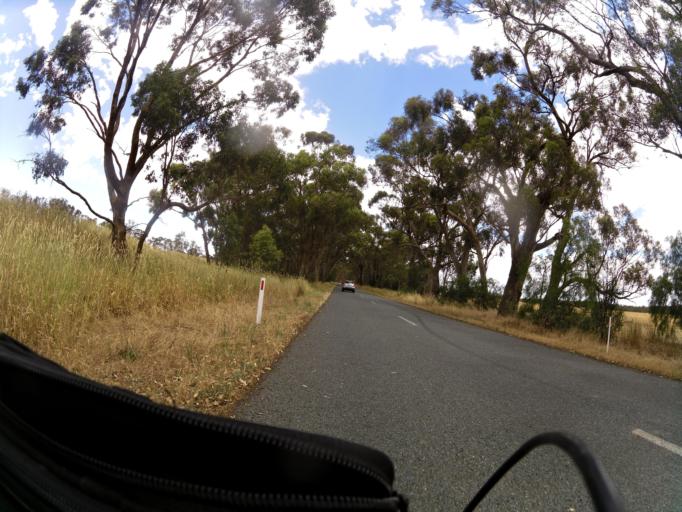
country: AU
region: Victoria
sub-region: Greater Shepparton
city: Shepparton
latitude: -36.6527
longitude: 145.2038
